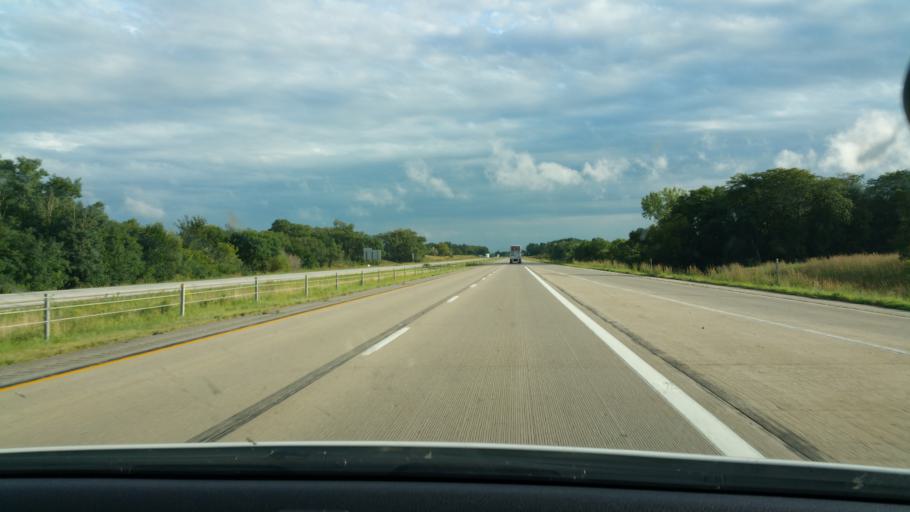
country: US
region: Iowa
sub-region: Story County
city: Story City
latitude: 42.1633
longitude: -93.5707
